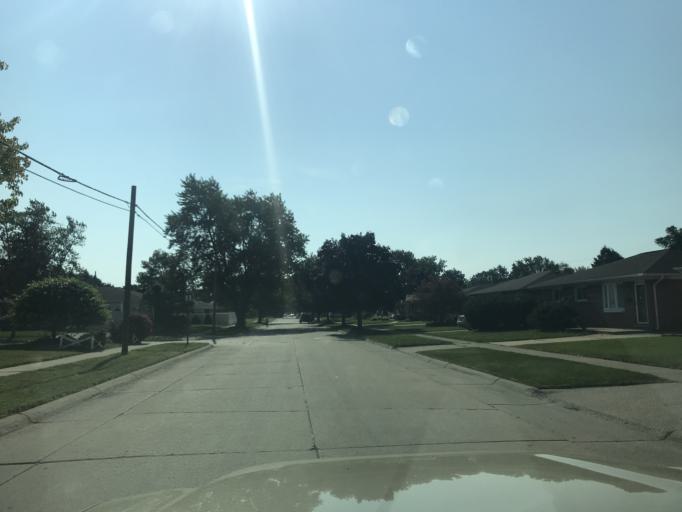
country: US
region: Michigan
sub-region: Wayne County
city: Melvindale
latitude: 42.2686
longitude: -83.1917
